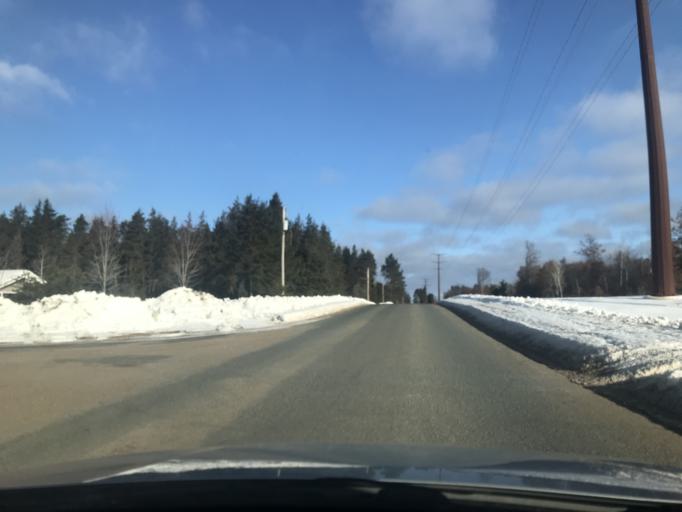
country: US
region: Wisconsin
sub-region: Marinette County
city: Niagara
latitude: 45.5980
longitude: -87.9769
